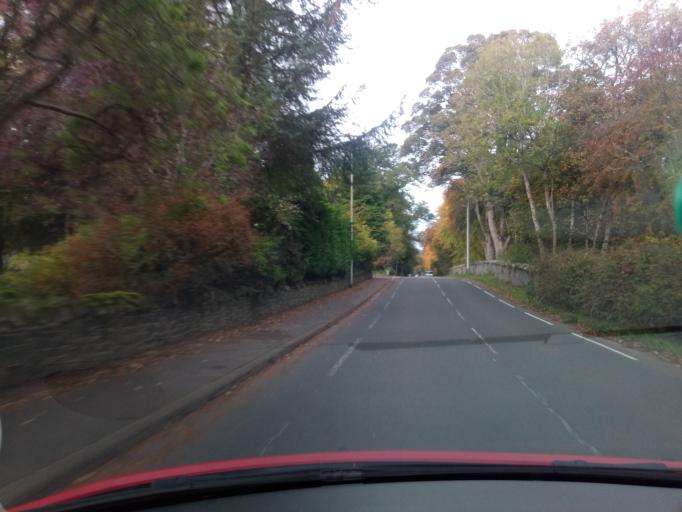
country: GB
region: Scotland
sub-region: The Scottish Borders
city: Peebles
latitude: 55.6454
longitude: -3.1752
